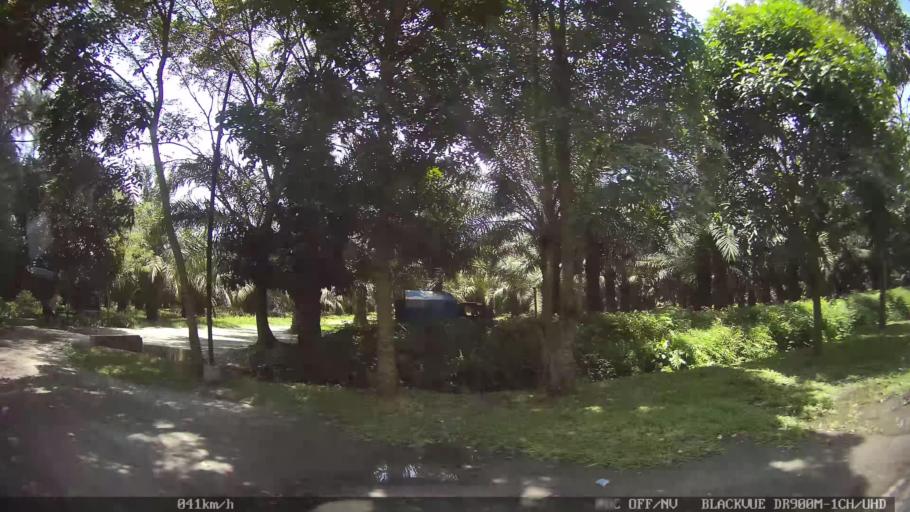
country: ID
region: North Sumatra
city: Percut
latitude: 3.5408
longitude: 98.8721
